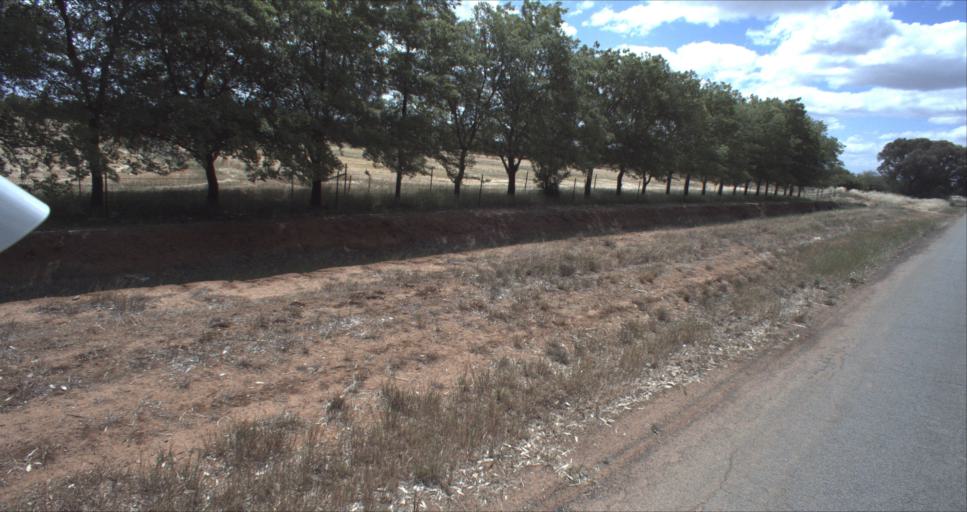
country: AU
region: New South Wales
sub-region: Leeton
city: Leeton
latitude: -34.5882
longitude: 146.3956
